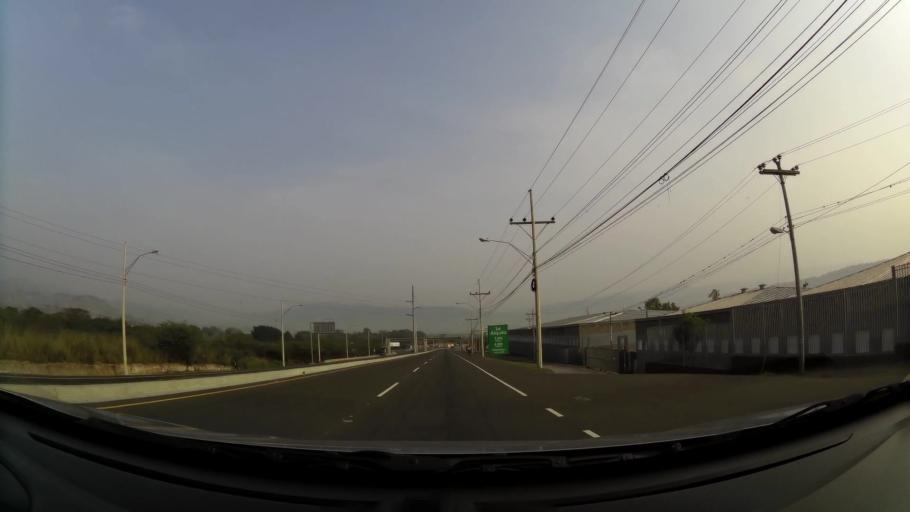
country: HN
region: Francisco Morazan
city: Tamara
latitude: 14.2074
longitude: -87.3506
